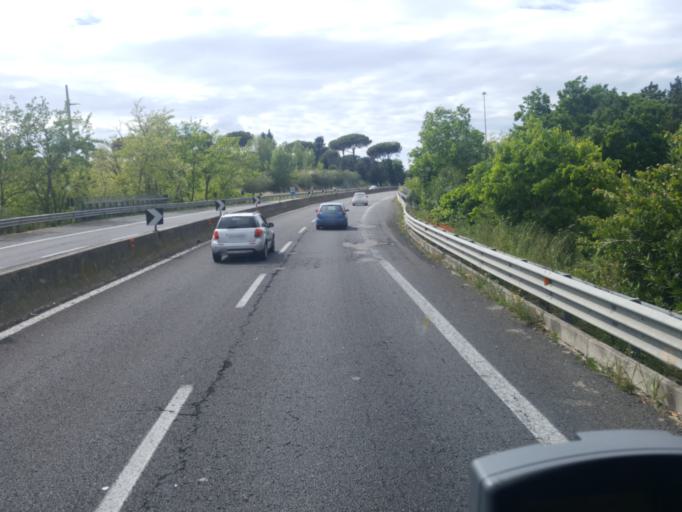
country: IT
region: Latium
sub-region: Citta metropolitana di Roma Capitale
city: Ara Nova
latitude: 41.9108
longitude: 12.2537
